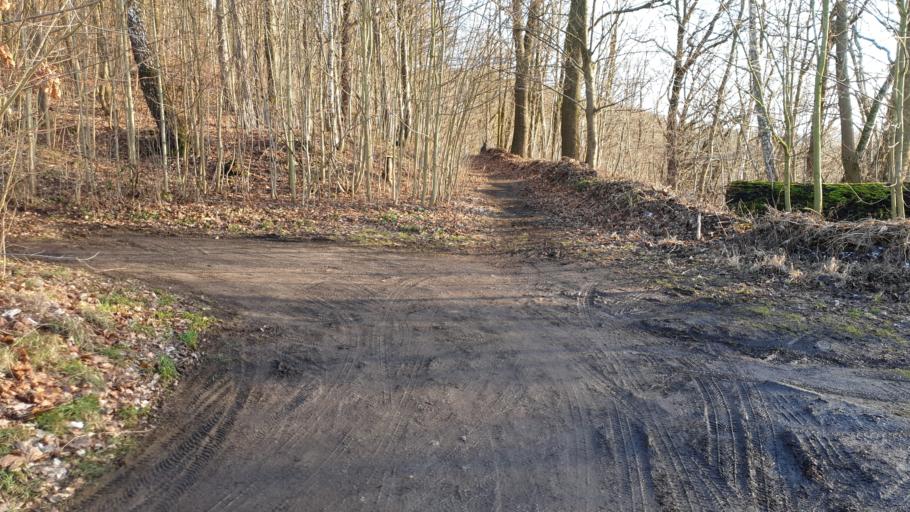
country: DE
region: Saxony
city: Gelenau
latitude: 50.7658
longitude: 12.9778
